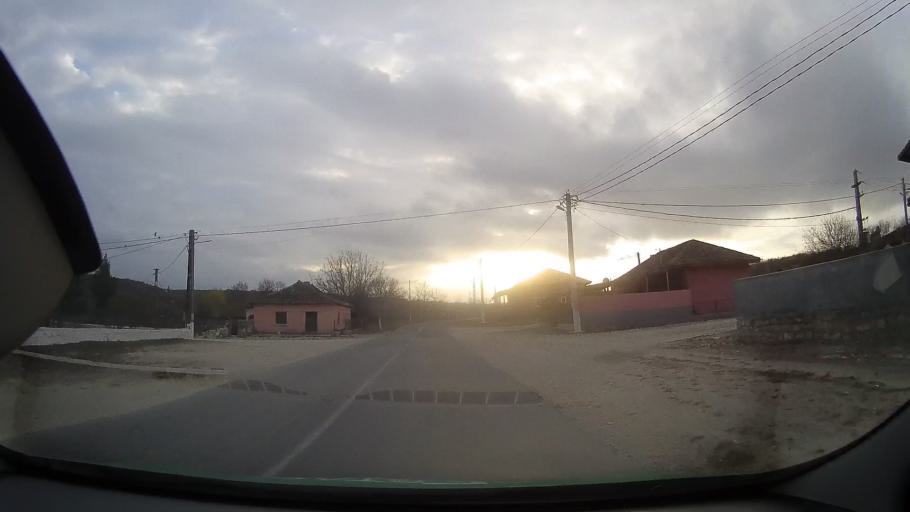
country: RO
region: Constanta
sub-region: Comuna Adamclisi
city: Adamclisi
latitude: 44.0442
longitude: 27.9579
